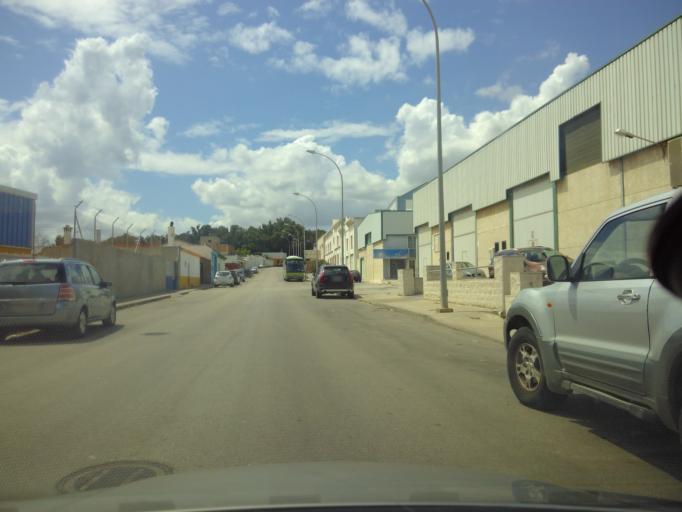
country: ES
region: Andalusia
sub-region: Provincia de Cadiz
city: La Linea de la Concepcion
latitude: 36.1827
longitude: -5.3502
